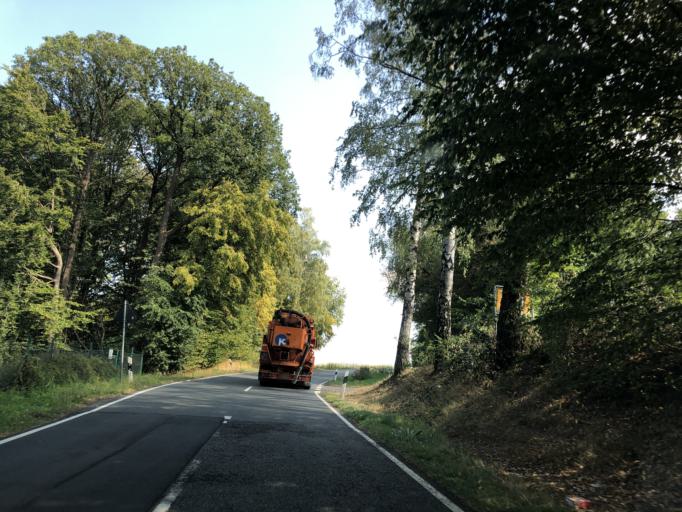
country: DE
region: Hesse
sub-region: Regierungsbezirk Giessen
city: Rauschenberg
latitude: 50.8759
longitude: 8.9532
